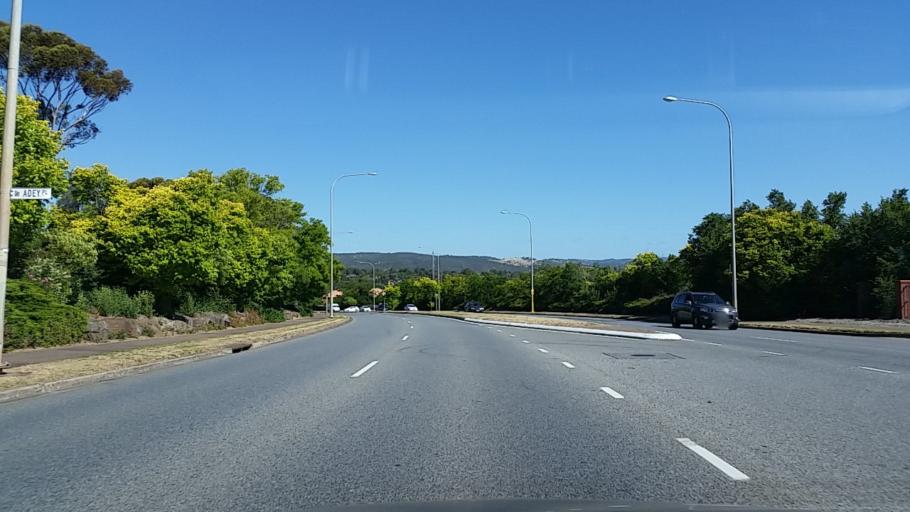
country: AU
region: South Australia
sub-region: Tea Tree Gully
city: Golden Grove
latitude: -34.7940
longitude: 138.6987
